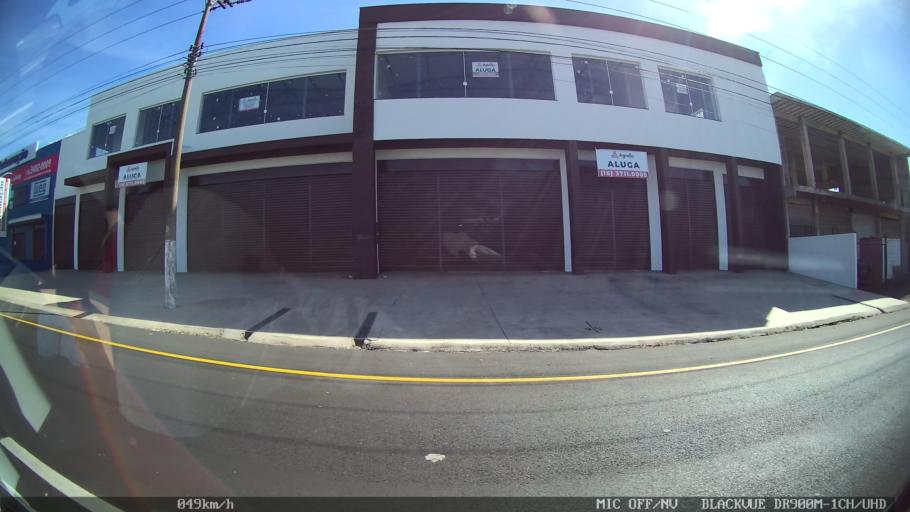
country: BR
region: Sao Paulo
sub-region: Franca
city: Franca
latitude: -20.5466
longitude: -47.4254
